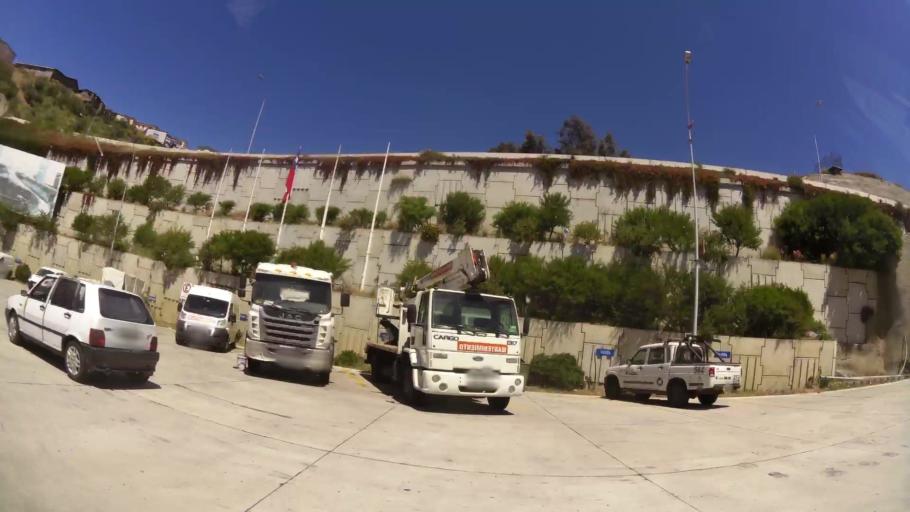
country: CL
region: Valparaiso
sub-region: Provincia de Valparaiso
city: Valparaiso
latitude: -33.0301
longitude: -71.6535
